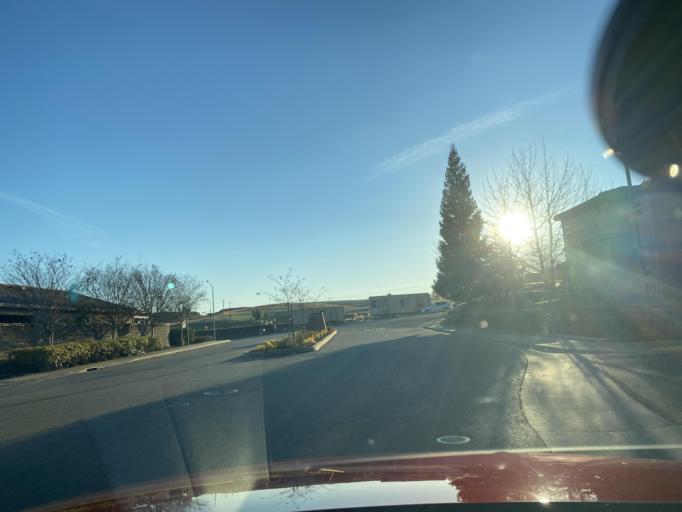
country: US
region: California
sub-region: El Dorado County
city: El Dorado Hills
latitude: 38.6492
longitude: -121.0896
